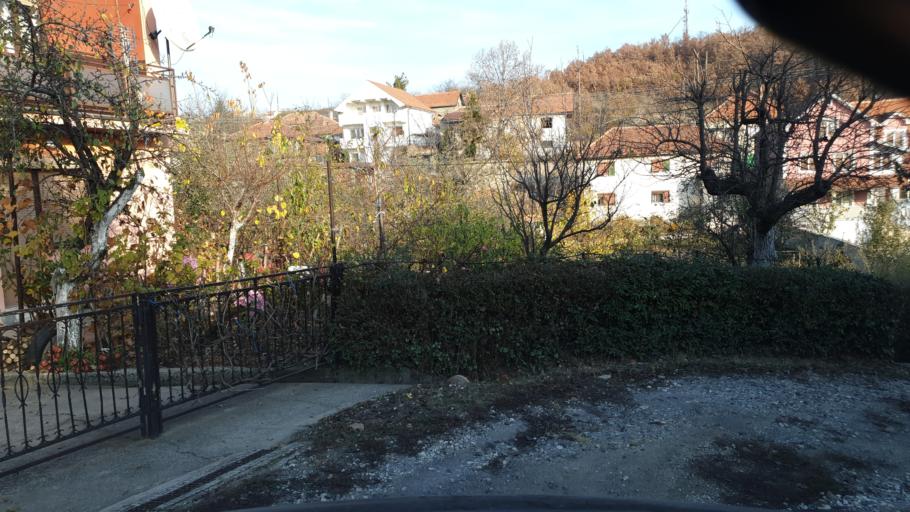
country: RS
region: Central Serbia
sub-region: Borski Okrug
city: Bor
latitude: 44.0519
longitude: 22.1020
